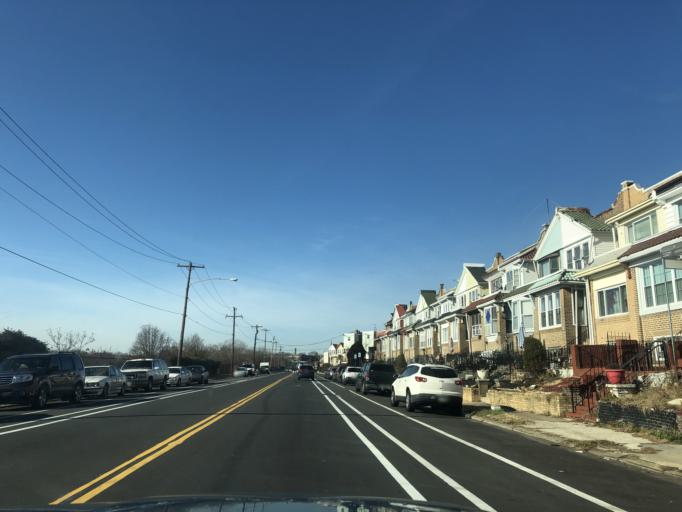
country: US
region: Pennsylvania
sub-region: Montgomery County
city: Bala-Cynwyd
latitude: 39.9829
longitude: -75.2318
